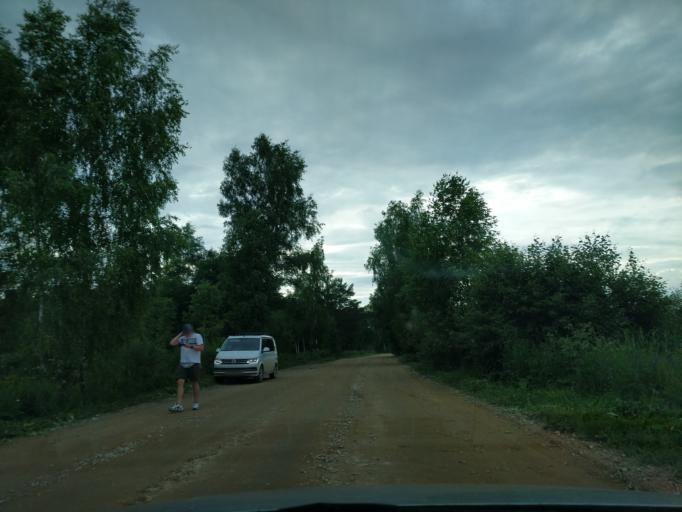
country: RU
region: Kaluga
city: Nikola-Lenivets
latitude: 54.7530
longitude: 35.6258
